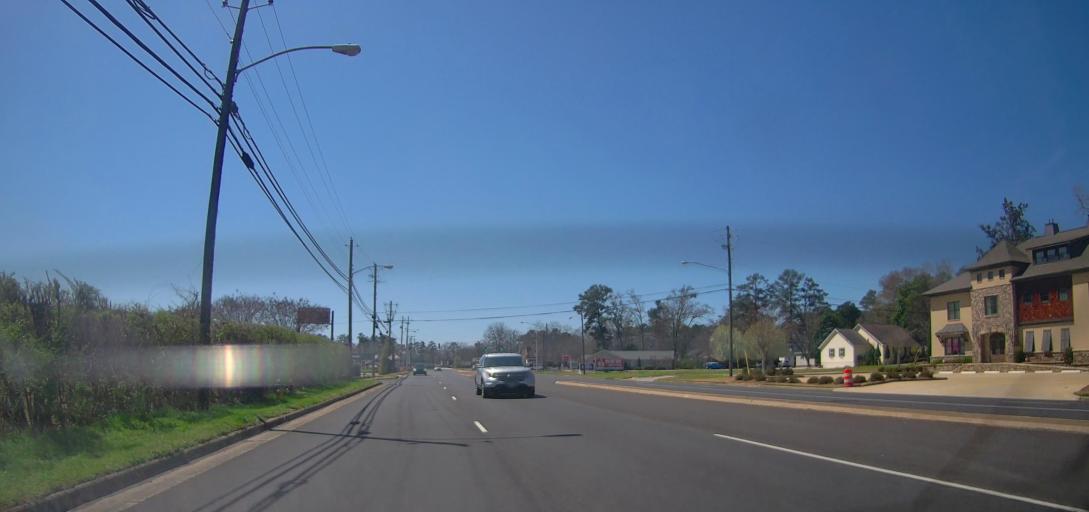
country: US
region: Alabama
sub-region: Etowah County
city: Rainbow City
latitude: 33.9760
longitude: -86.0127
